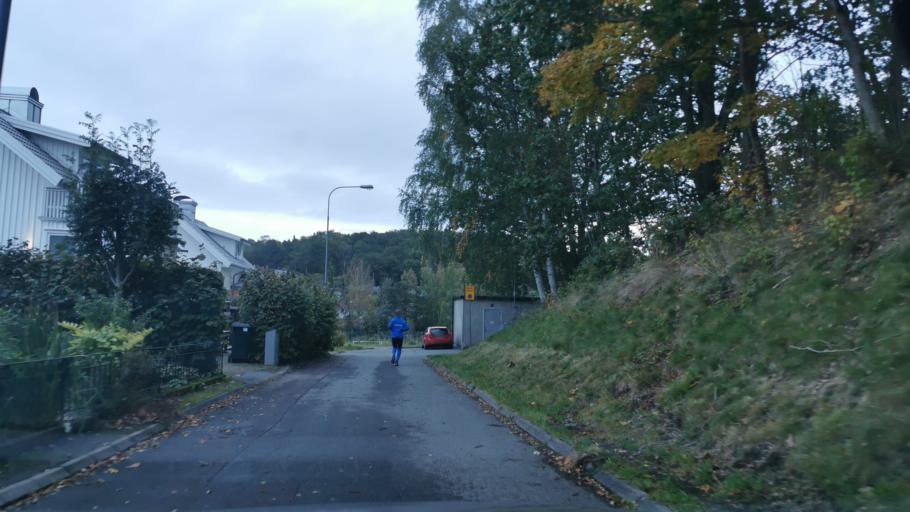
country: SE
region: Vaestra Goetaland
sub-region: Partille Kommun
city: Partille
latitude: 57.7243
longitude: 12.0818
